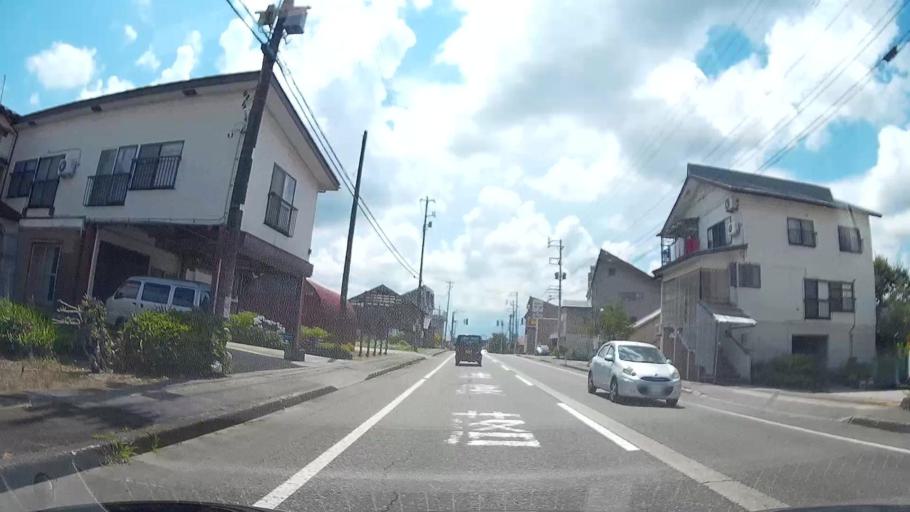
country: JP
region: Niigata
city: Tokamachi
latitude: 37.0570
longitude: 138.7026
